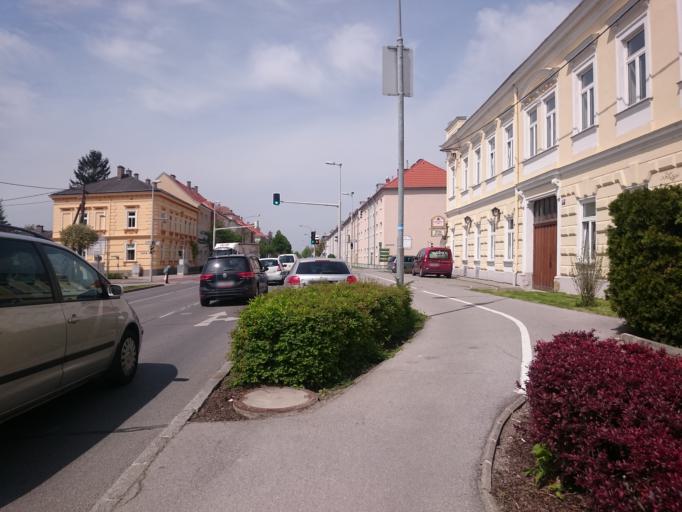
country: AT
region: Lower Austria
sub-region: Politischer Bezirk Korneuburg
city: Korneuburg
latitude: 48.3480
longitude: 16.3284
